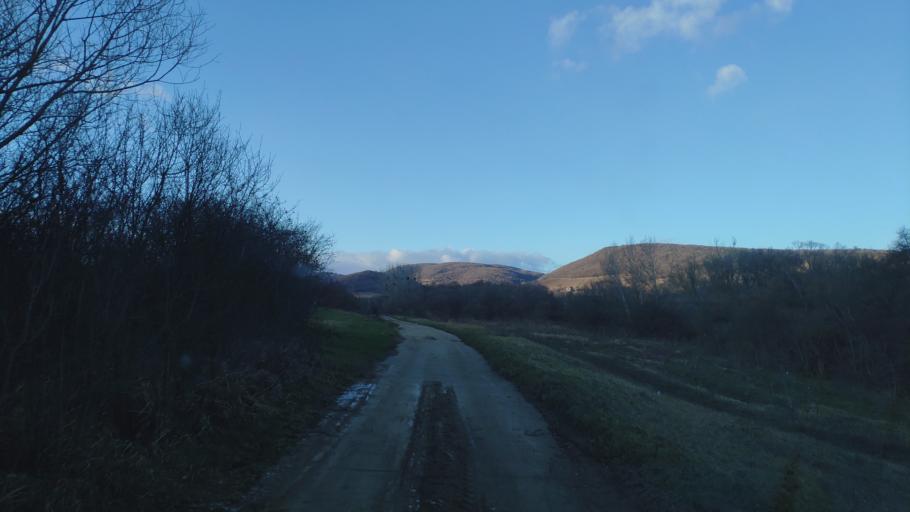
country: HU
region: Borsod-Abauj-Zemplen
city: Tolcsva
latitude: 48.2808
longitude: 21.4900
